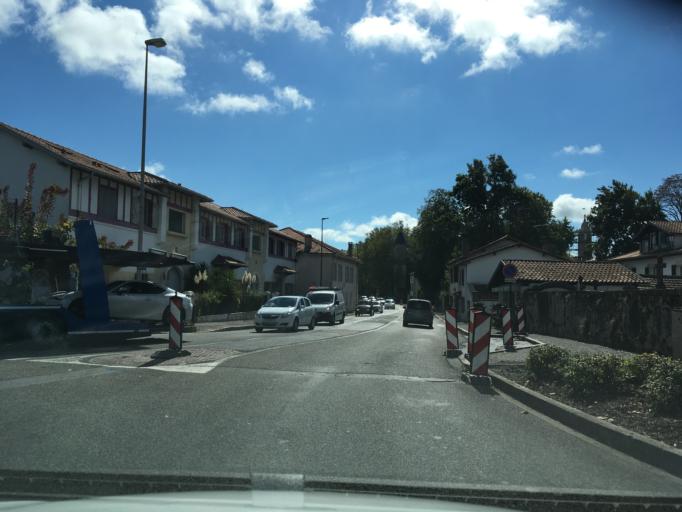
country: FR
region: Aquitaine
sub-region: Departement des Pyrenees-Atlantiques
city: Boucau
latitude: 43.5033
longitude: -1.4640
